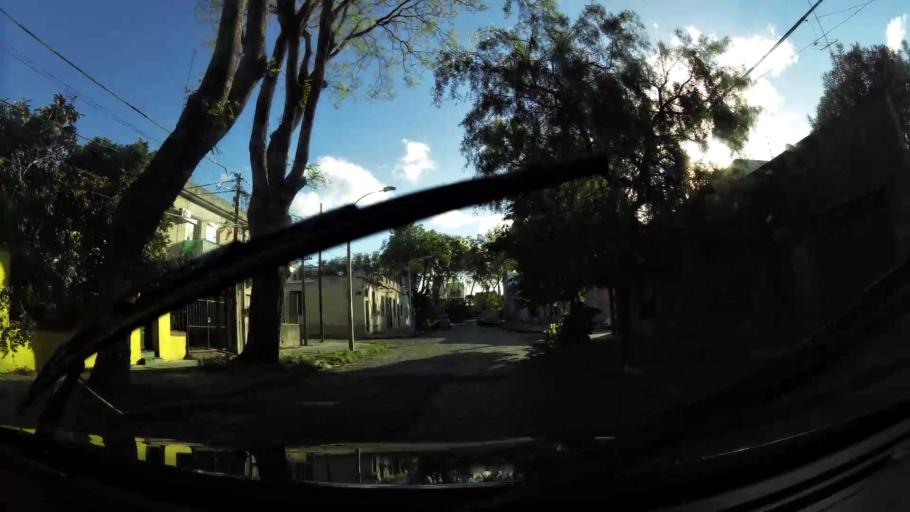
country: UY
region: Montevideo
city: Montevideo
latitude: -34.8846
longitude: -56.1313
